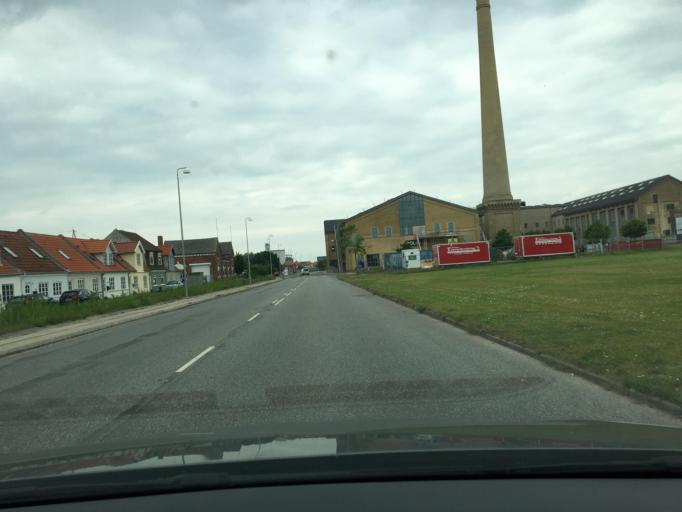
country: DK
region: South Denmark
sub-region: Assens Kommune
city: Assens
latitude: 55.2647
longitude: 9.8924
